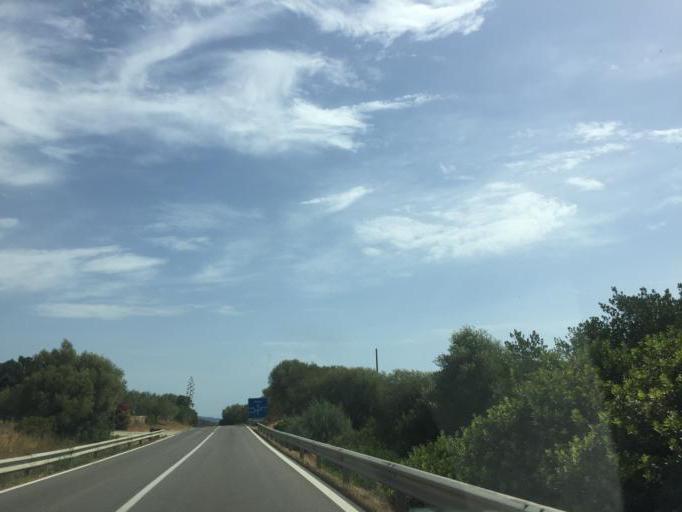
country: IT
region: Sardinia
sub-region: Provincia di Olbia-Tempio
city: San Teodoro
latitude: 40.7535
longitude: 9.6489
